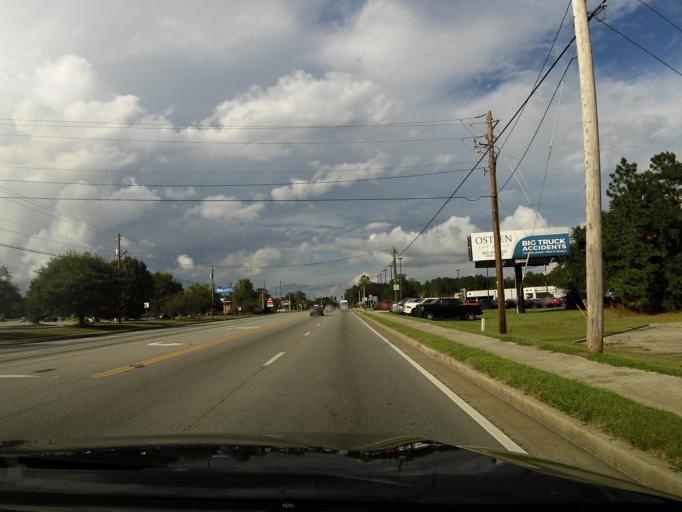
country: US
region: Georgia
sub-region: Liberty County
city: Hinesville
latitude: 31.8247
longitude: -81.5989
